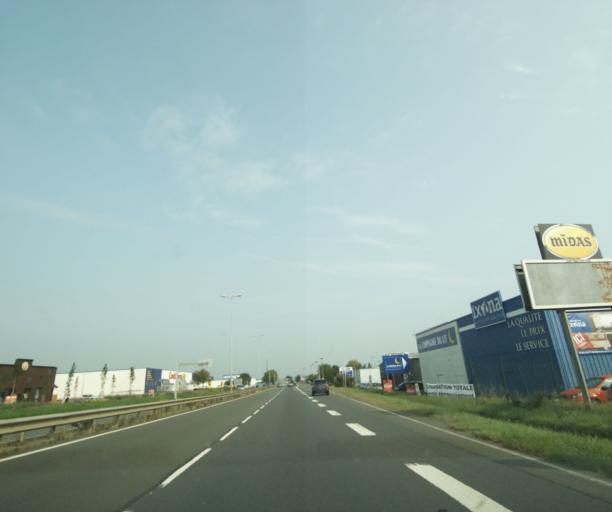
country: FR
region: Pays de la Loire
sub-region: Departement de la Sarthe
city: La Chapelle-Saint-Aubin
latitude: 48.0374
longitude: 0.1760
